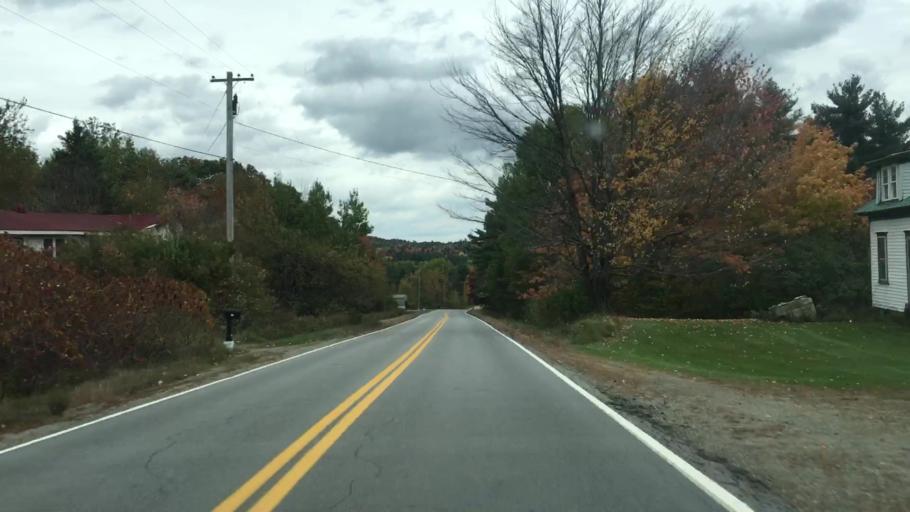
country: US
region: Maine
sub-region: Waldo County
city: Brooks
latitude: 44.5860
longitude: -69.0837
